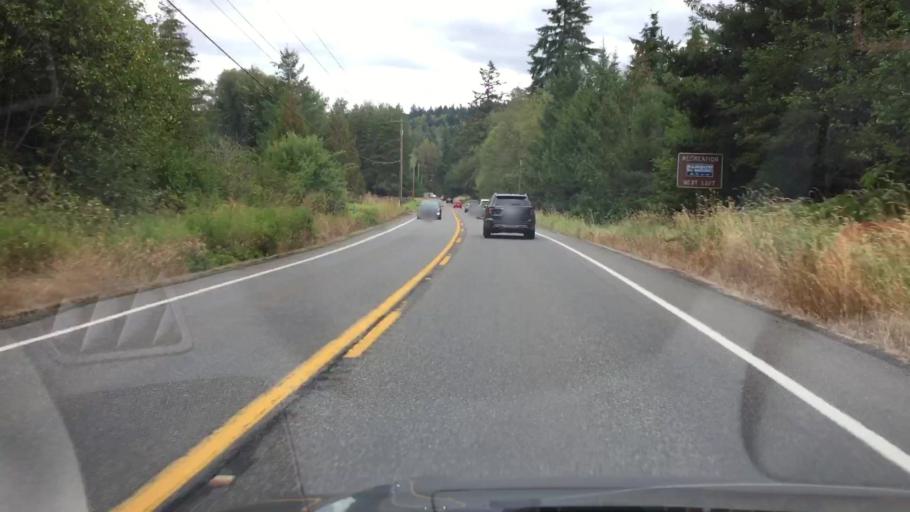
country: US
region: Washington
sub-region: Pierce County
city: Eatonville
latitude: 46.9449
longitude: -122.2868
